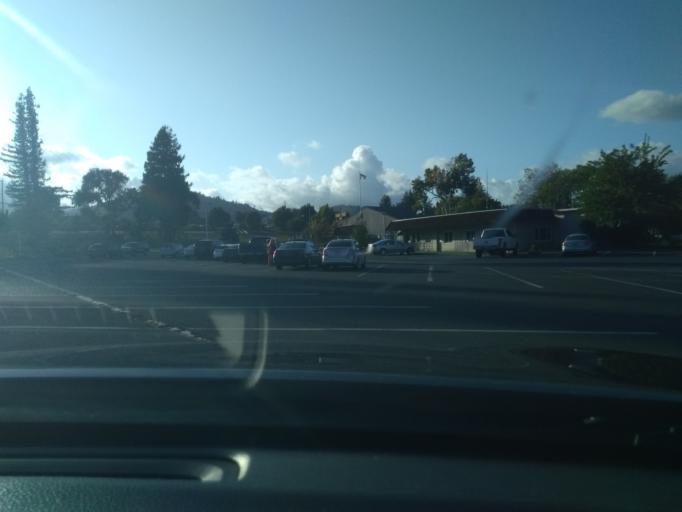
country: US
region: California
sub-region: Mendocino County
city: Ukiah
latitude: 39.1625
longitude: -123.2075
